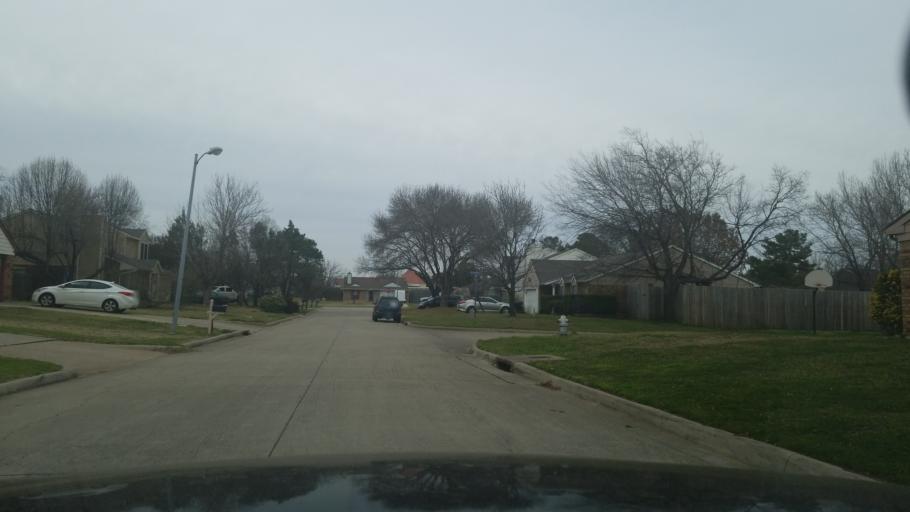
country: US
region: Texas
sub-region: Denton County
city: Hickory Creek
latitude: 33.1346
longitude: -97.0512
